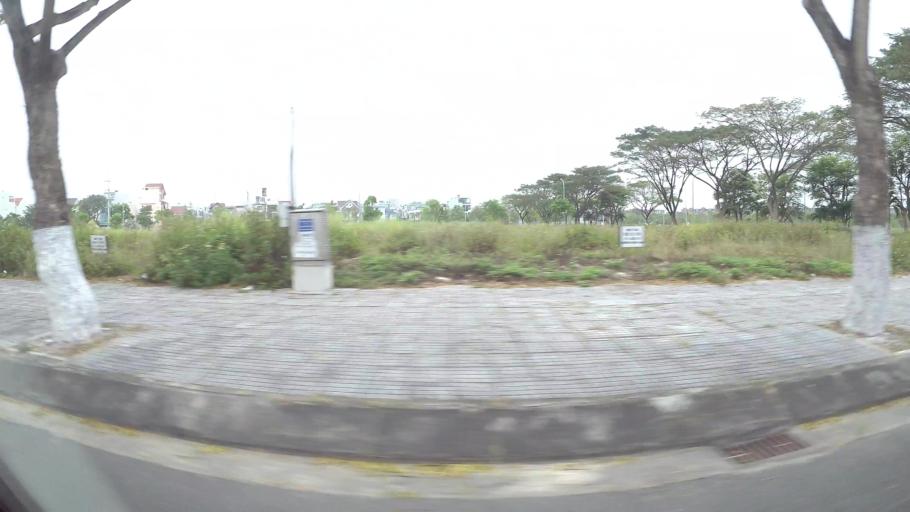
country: VN
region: Da Nang
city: Ngu Hanh Son
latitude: 16.0324
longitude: 108.2334
